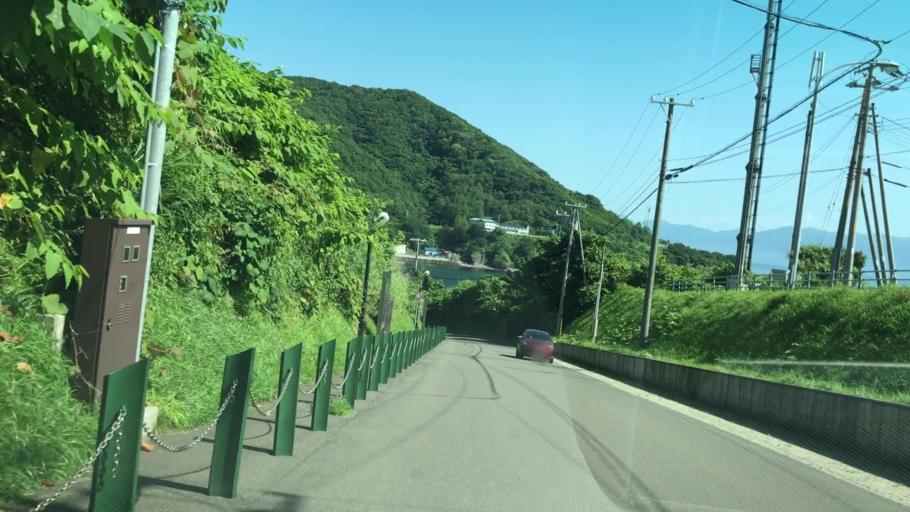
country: JP
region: Hokkaido
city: Iwanai
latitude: 43.1442
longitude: 140.4253
